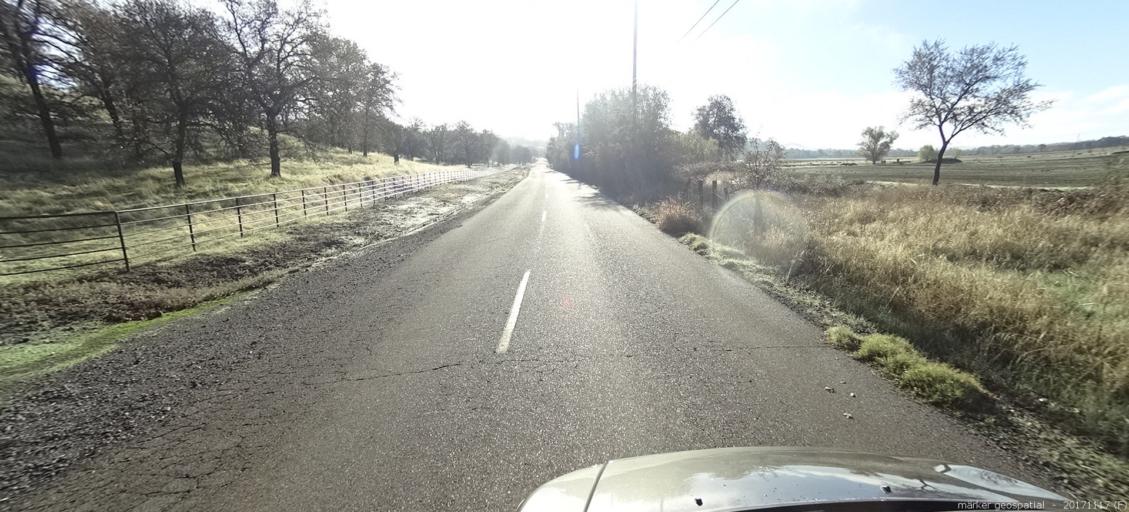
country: US
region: California
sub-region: Shasta County
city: Cottonwood
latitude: 40.4121
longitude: -122.1883
